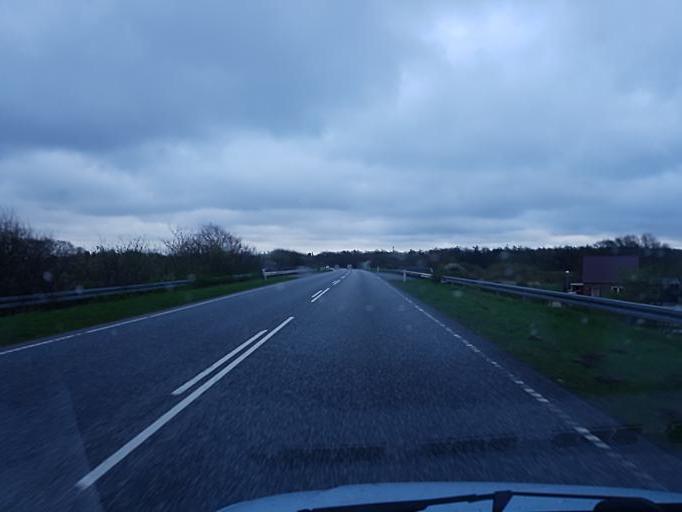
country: DK
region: South Denmark
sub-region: Esbjerg Kommune
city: Ribe
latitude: 55.3959
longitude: 8.7323
